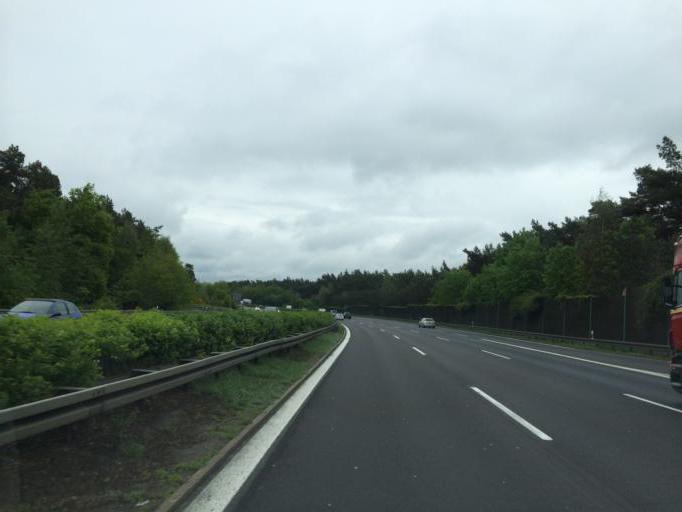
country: DE
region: Brandenburg
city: Michendorf
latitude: 52.2991
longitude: 13.0289
